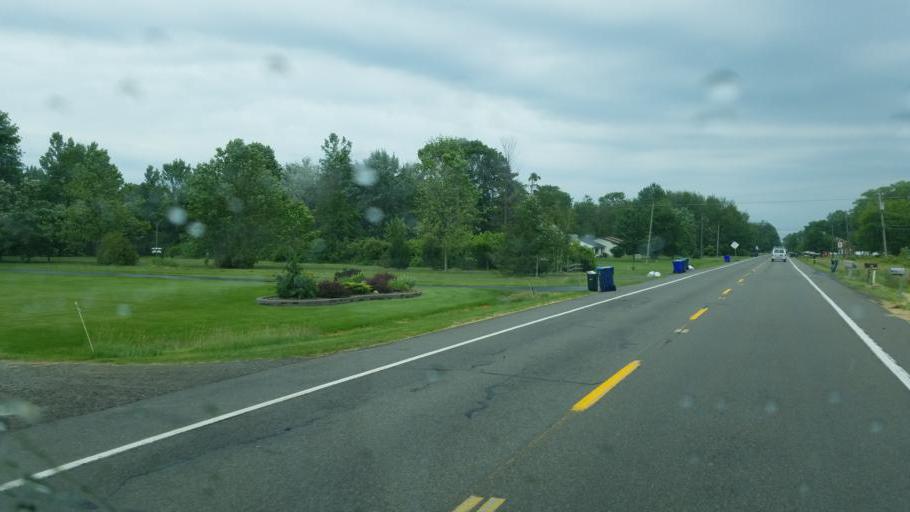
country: US
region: New York
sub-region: Niagara County
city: Ransomville
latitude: 43.2792
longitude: -78.9704
